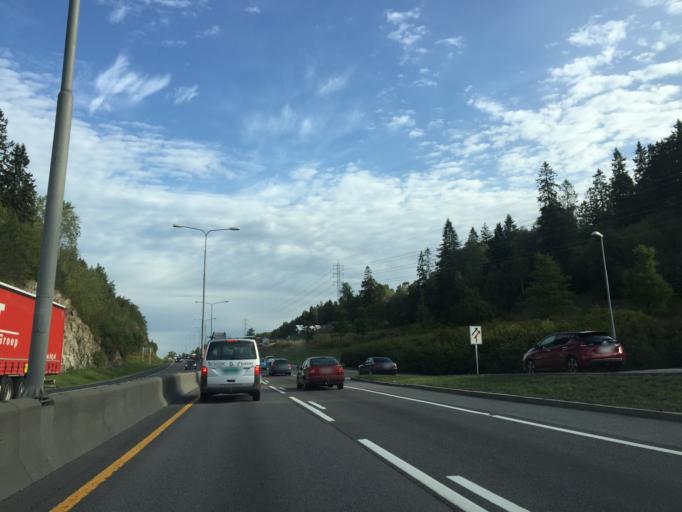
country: NO
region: Akershus
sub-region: Oppegard
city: Kolbotn
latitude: 59.8636
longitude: 10.8308
